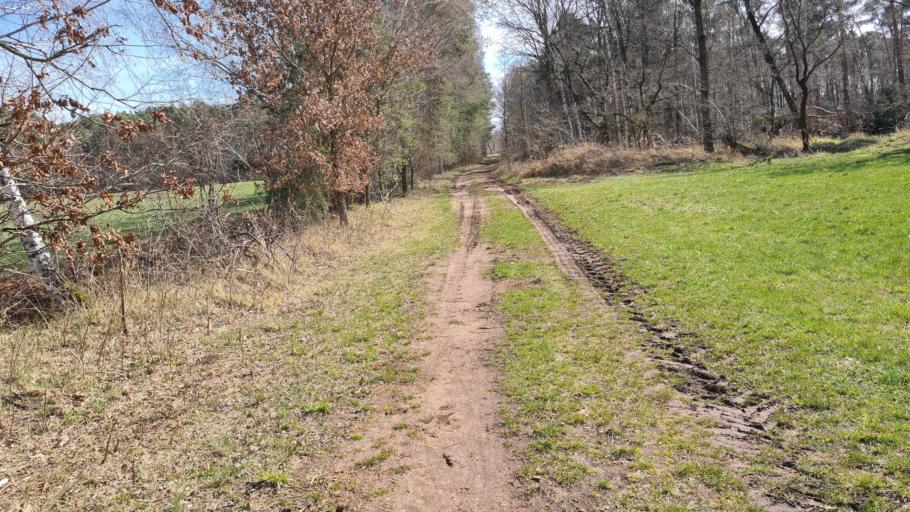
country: DE
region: Brandenburg
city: Finsterwalde
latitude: 51.6020
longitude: 13.6424
